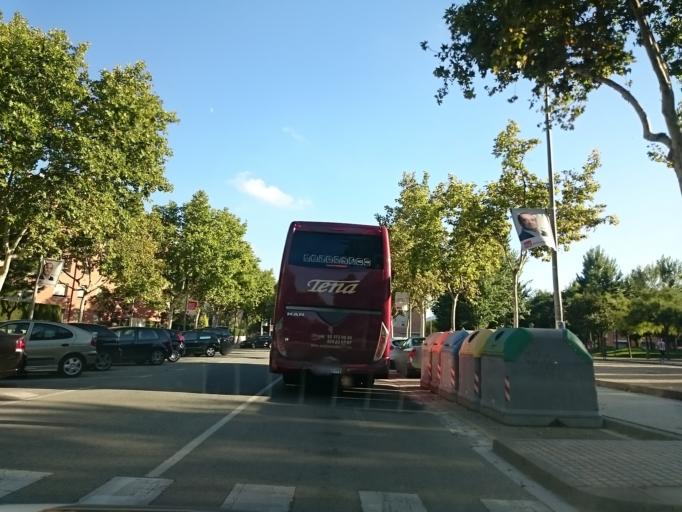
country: ES
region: Catalonia
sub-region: Provincia de Barcelona
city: Palleja
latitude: 41.4235
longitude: 1.9998
